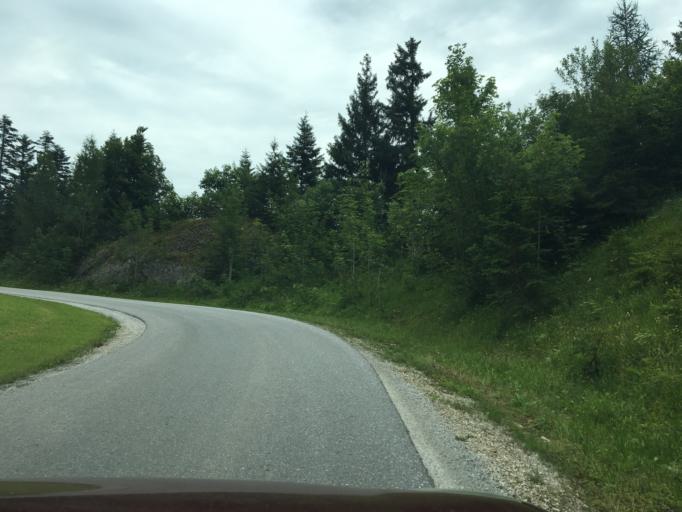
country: AT
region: Salzburg
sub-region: Politischer Bezirk Hallein
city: Abtenau
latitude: 47.6023
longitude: 13.3657
